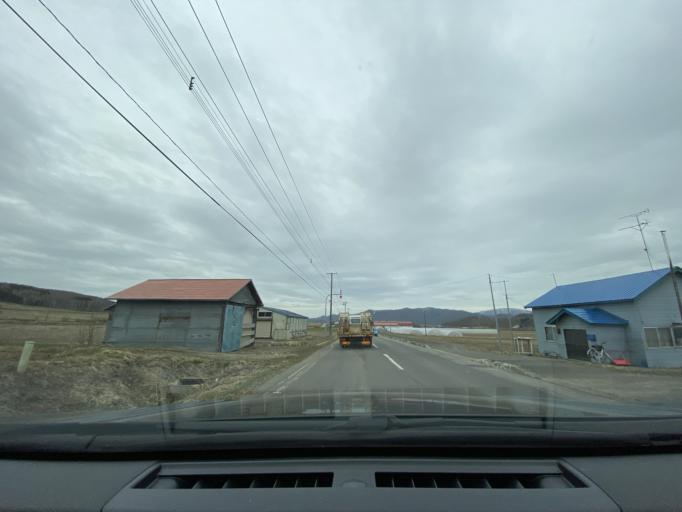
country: JP
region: Hokkaido
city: Nayoro
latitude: 44.0958
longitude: 142.4741
